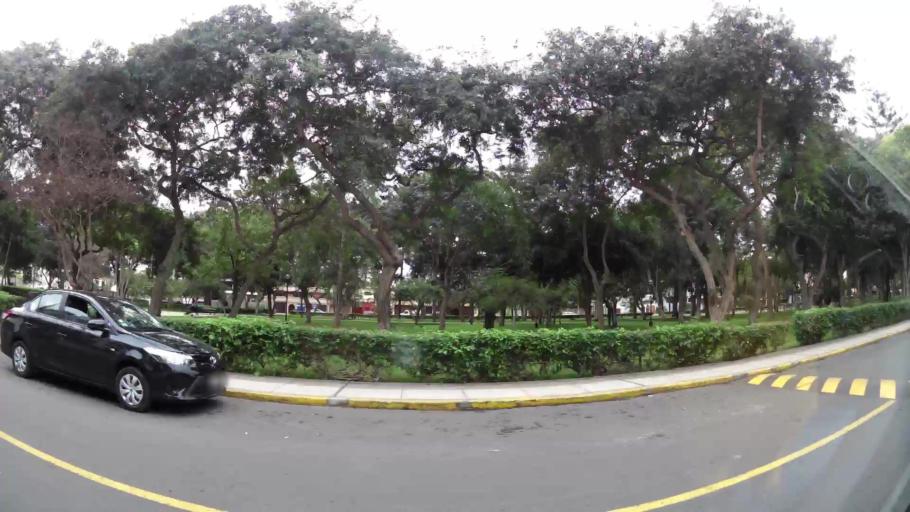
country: PE
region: Lima
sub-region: Lima
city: Surco
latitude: -12.1223
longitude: -77.0164
